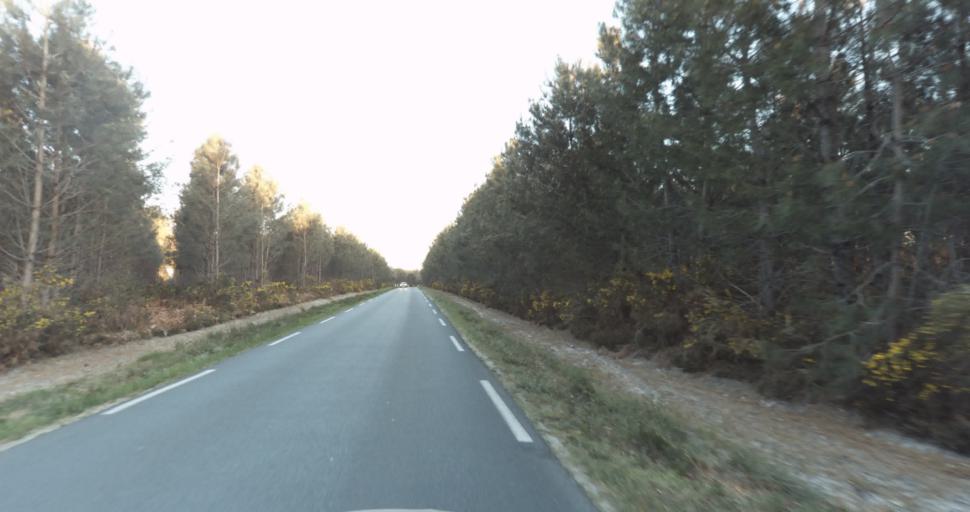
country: FR
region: Aquitaine
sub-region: Departement de la Gironde
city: Martignas-sur-Jalle
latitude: 44.8259
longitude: -0.7598
